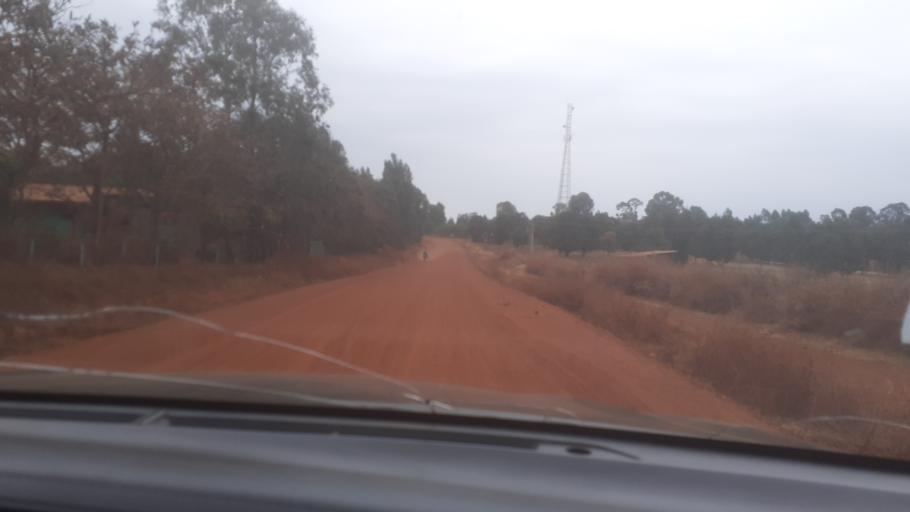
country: ET
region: Binshangul Gumuz
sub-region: Asosa
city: Asosa
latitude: 10.0982
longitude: 34.6000
